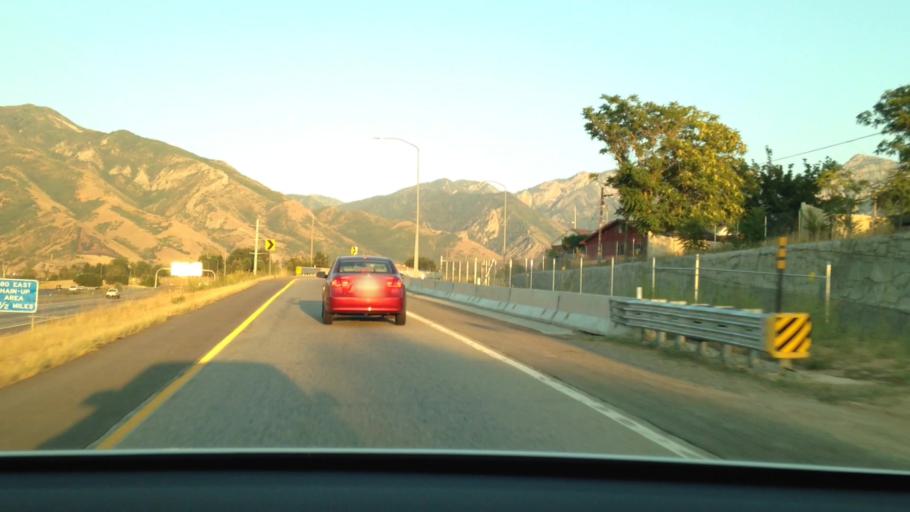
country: US
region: Utah
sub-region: Salt Lake County
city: Canyon Rim
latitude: 40.7133
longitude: -111.8260
